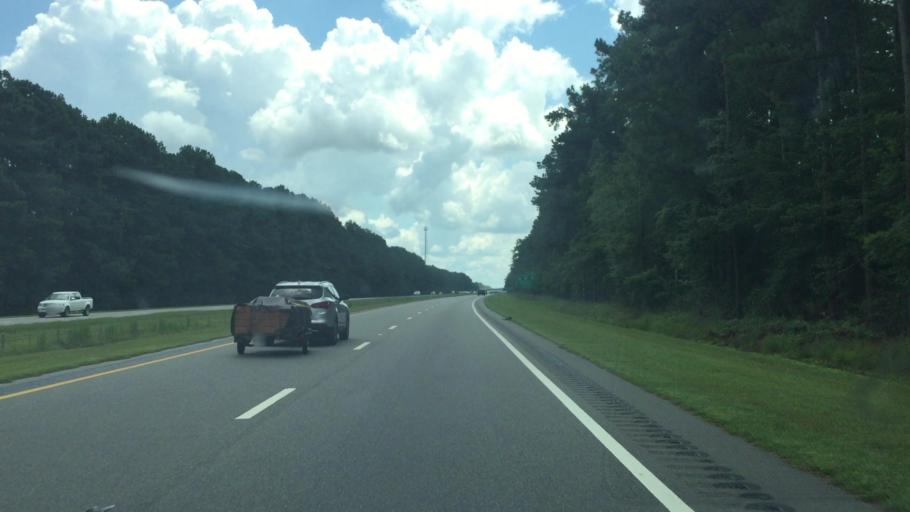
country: US
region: North Carolina
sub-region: Columbus County
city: Chadbourn
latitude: 34.3754
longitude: -78.8470
